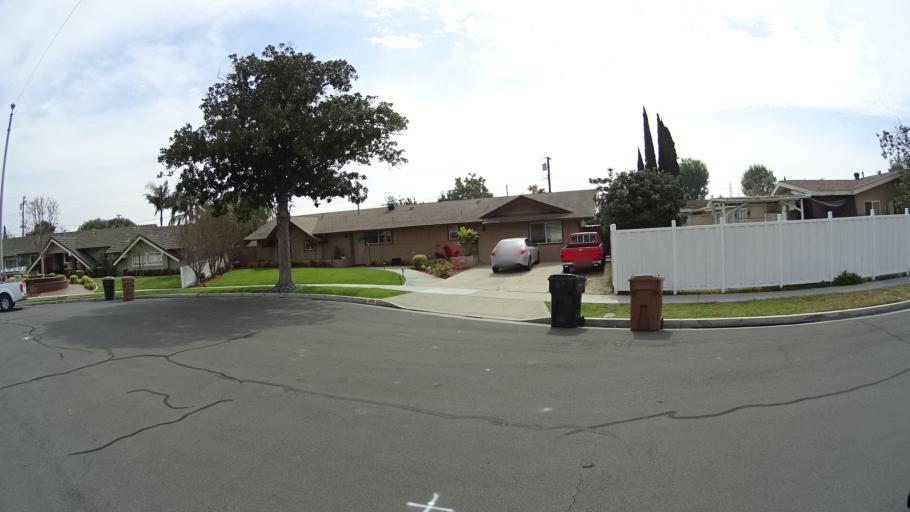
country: US
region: California
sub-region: Orange County
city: Garden Grove
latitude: 33.8114
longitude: -117.9483
